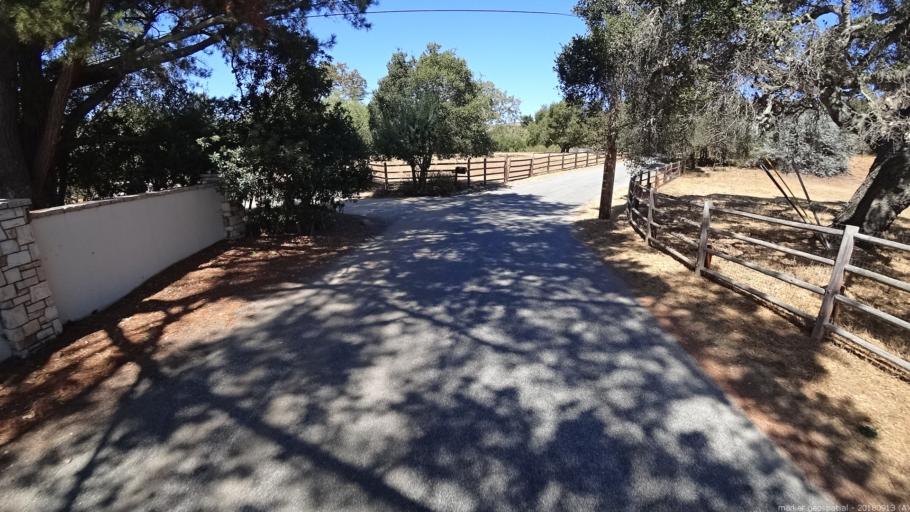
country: US
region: California
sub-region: Monterey County
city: Carmel Valley Village
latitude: 36.5072
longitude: -121.7580
